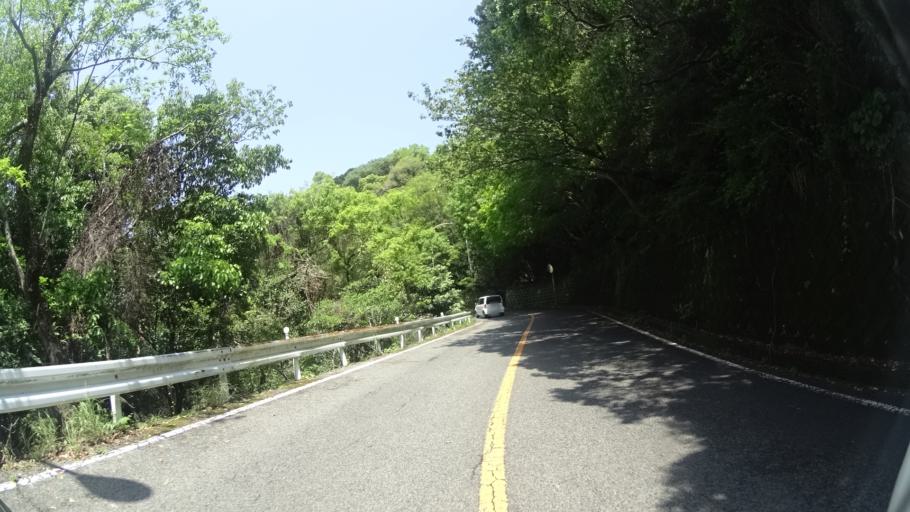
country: JP
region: Tokushima
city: Tokushima-shi
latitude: 34.0655
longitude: 134.5332
